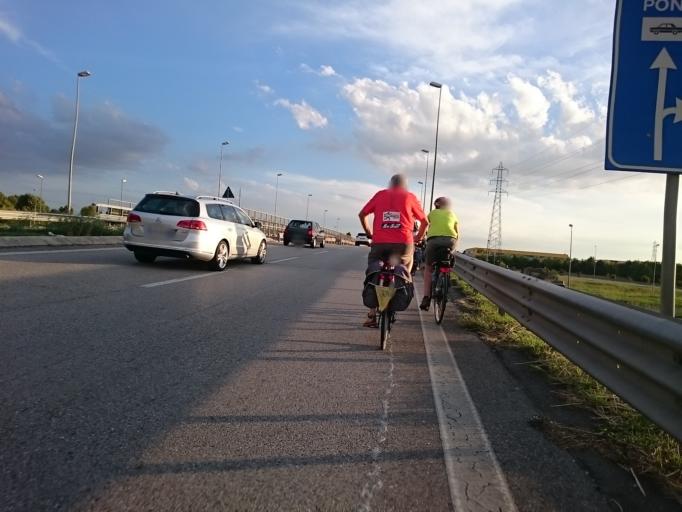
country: IT
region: Veneto
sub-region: Provincia di Padova
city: Ponte San Nicolo
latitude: 45.3829
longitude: 11.9395
